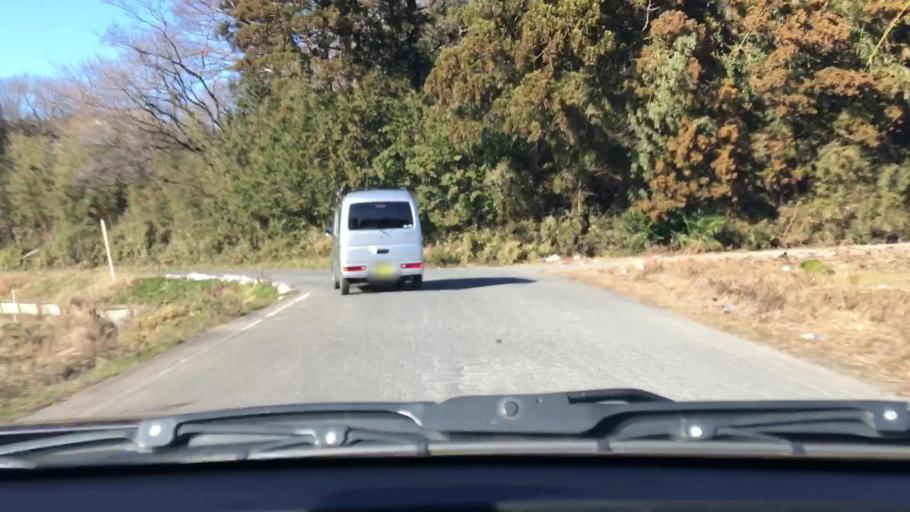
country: JP
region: Chiba
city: Shisui
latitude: 35.7028
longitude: 140.2870
